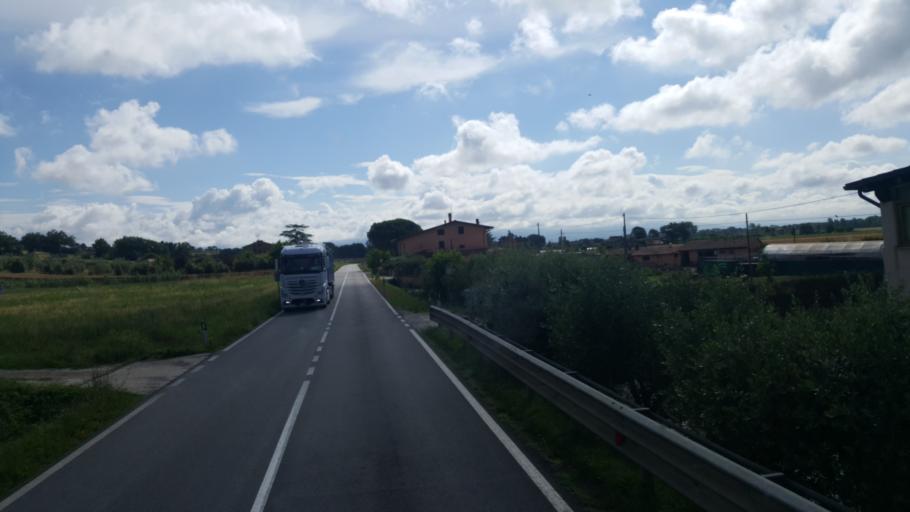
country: IT
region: Umbria
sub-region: Provincia di Perugia
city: Torgiano
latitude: 43.0365
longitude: 12.4539
